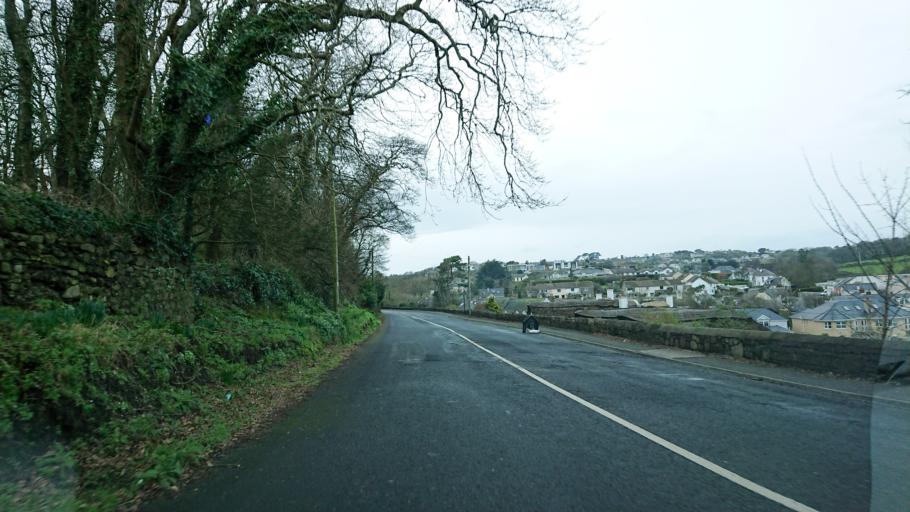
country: IE
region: Munster
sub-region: Waterford
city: Dunmore East
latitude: 52.1540
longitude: -6.9948
